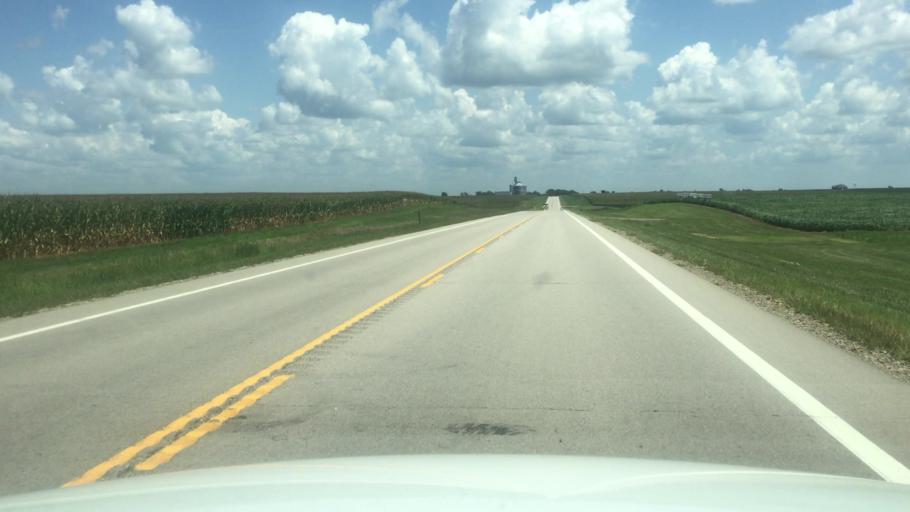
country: US
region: Kansas
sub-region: Brown County
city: Horton
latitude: 39.6602
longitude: -95.4021
